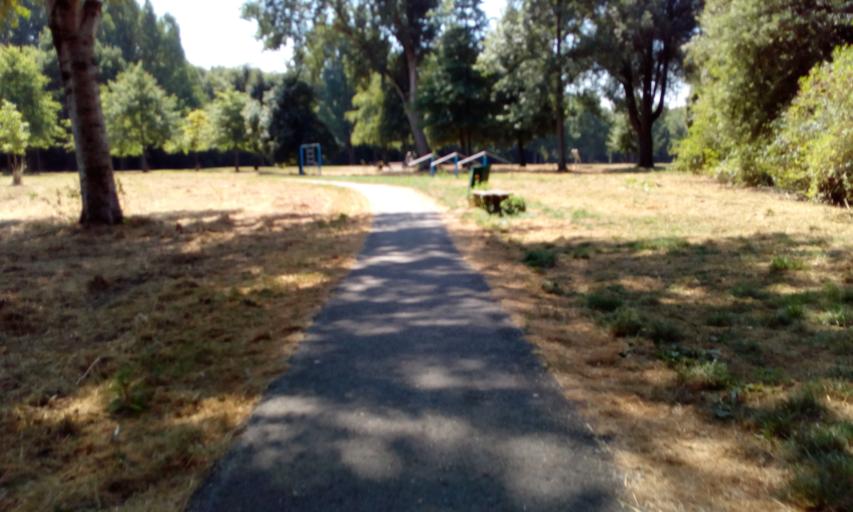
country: NL
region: South Holland
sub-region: Gemeente Capelle aan den IJssel
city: Capelle aan den IJssel
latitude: 51.9471
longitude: 4.5848
